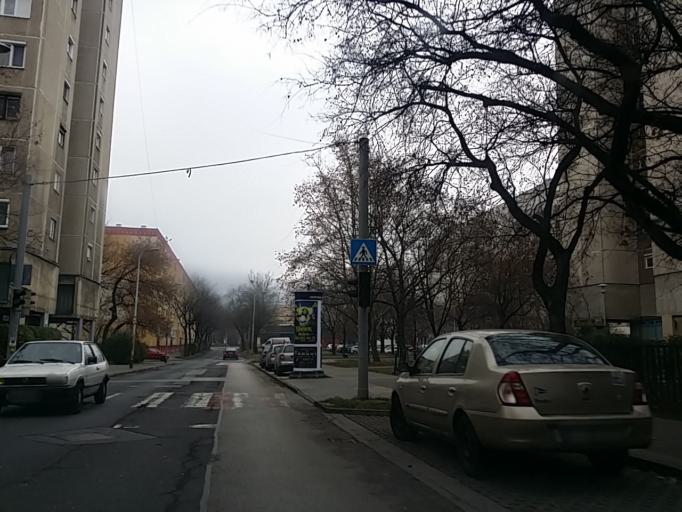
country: HU
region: Budapest
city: Budapest III. keruelet
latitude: 47.5458
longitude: 19.0406
